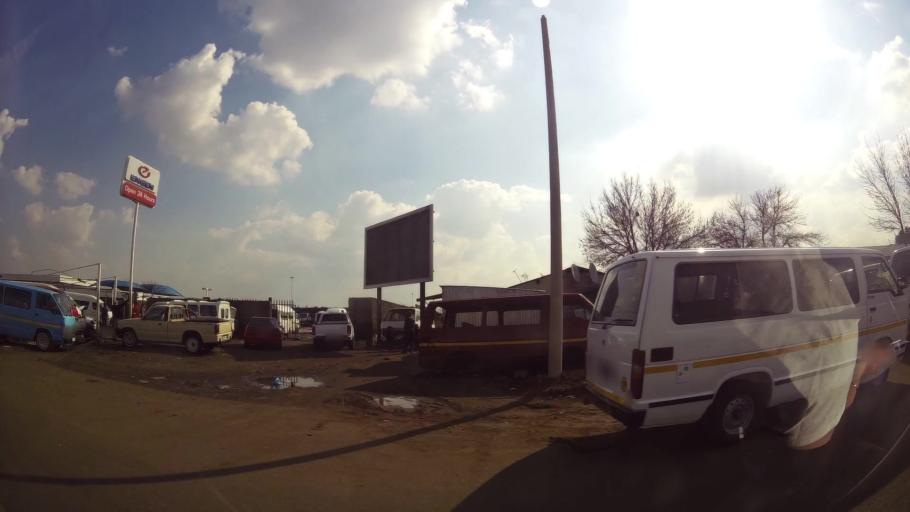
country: ZA
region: Gauteng
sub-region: Ekurhuleni Metropolitan Municipality
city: Germiston
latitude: -26.3401
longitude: 28.1393
